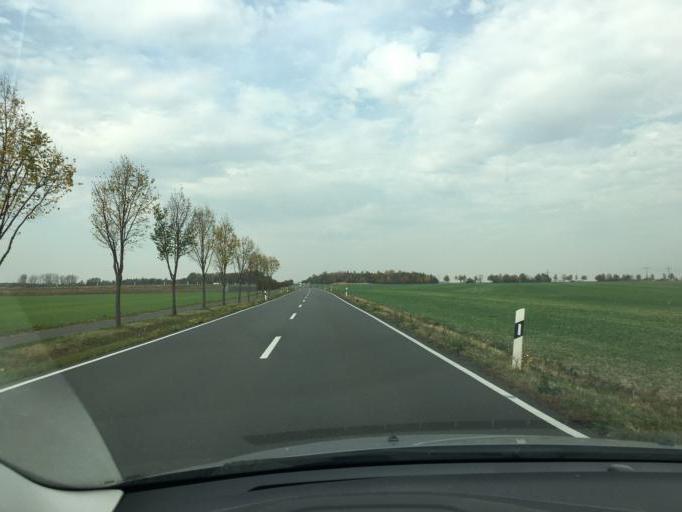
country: DE
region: Saxony
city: Zwochau
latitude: 51.4308
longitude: 12.2843
